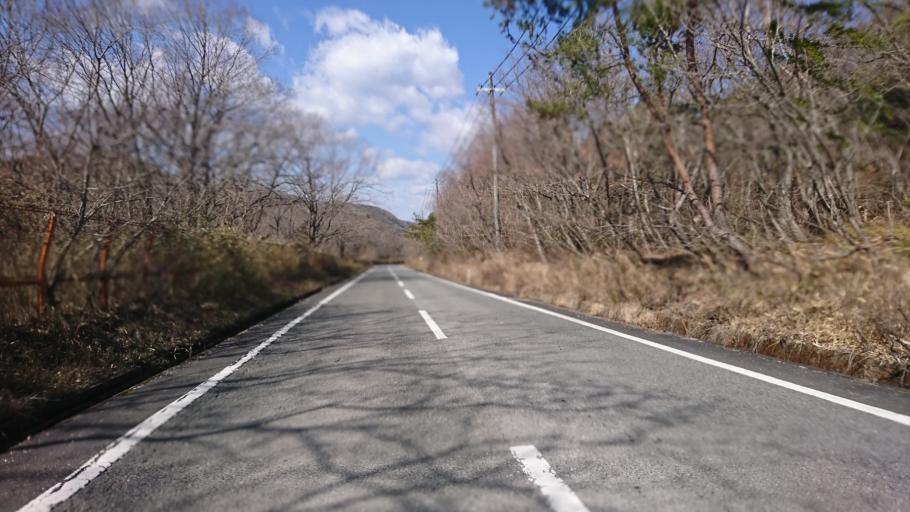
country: JP
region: Hyogo
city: Kakogawacho-honmachi
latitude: 34.8607
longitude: 134.8012
